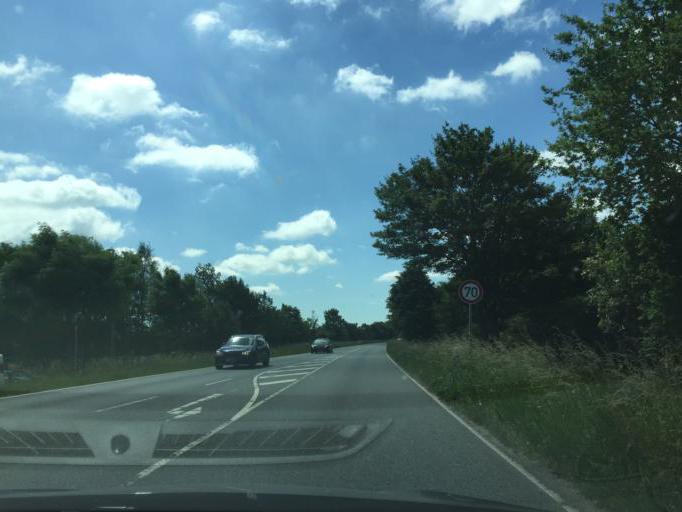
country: DE
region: Schleswig-Holstein
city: Harrislee
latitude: 54.7936
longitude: 9.3721
